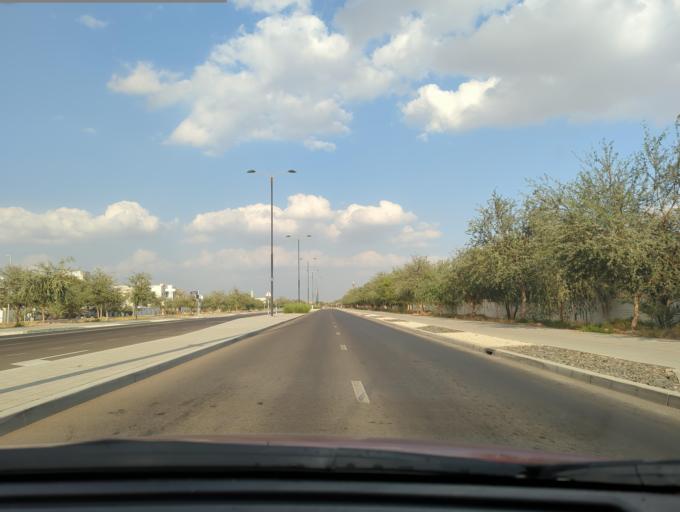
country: AE
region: Abu Dhabi
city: Al Ain
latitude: 24.1569
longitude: 55.6644
